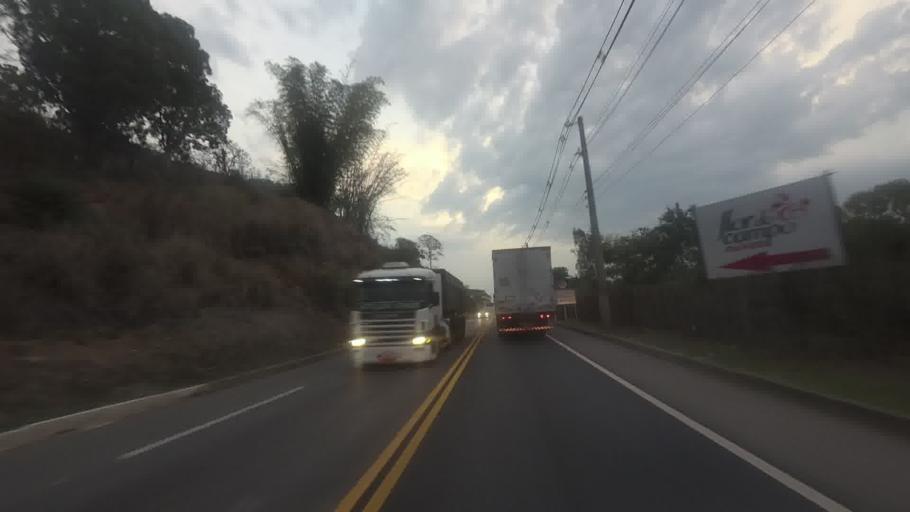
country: BR
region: Minas Gerais
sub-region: Alem Paraiba
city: Alem Paraiba
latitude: -21.8784
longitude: -42.6778
